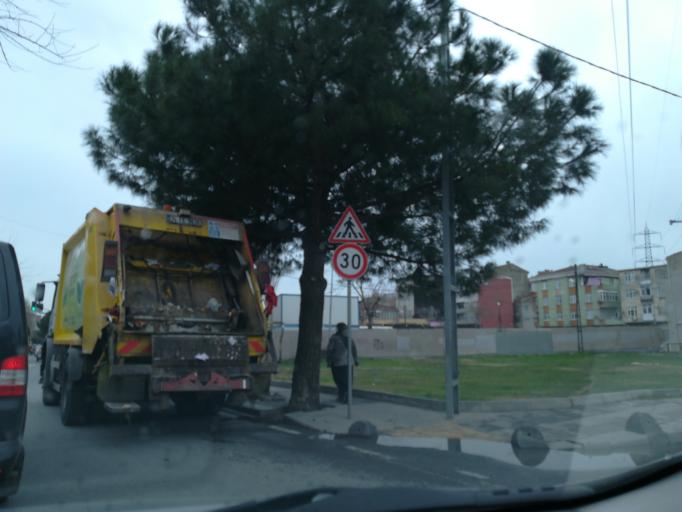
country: TR
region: Istanbul
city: Bagcilar
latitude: 41.0354
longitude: 28.8431
